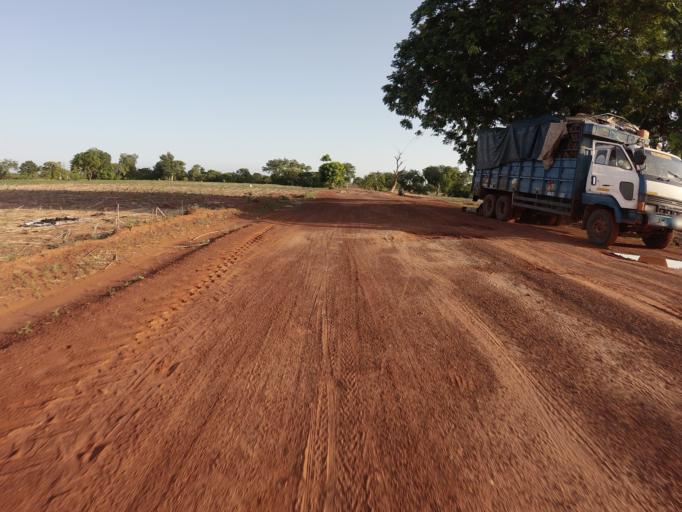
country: TG
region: Savanes
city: Sansanne-Mango
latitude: 10.3424
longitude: -0.0927
